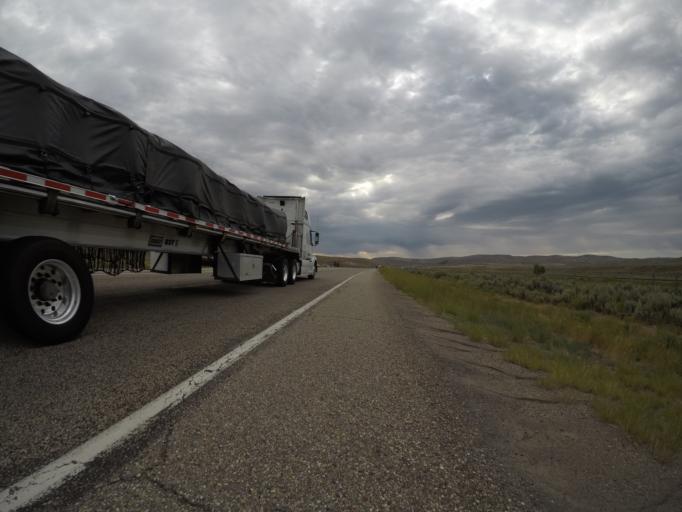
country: US
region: Utah
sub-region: Rich County
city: Randolph
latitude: 41.8255
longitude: -110.9179
